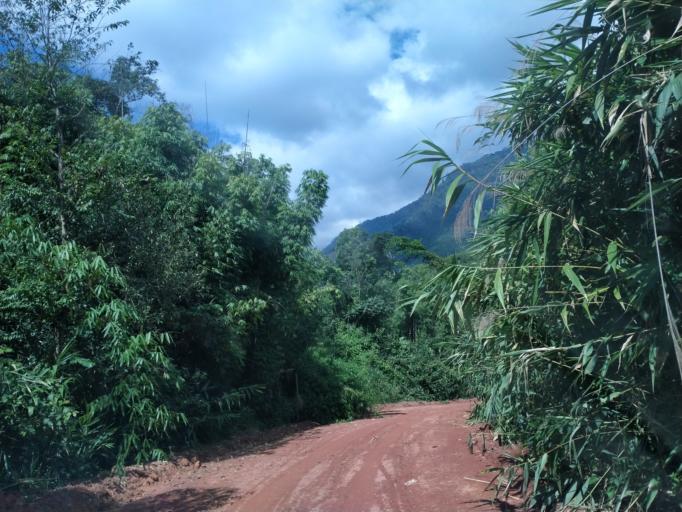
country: LA
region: Vientiane
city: Muang Phon-Hong
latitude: 18.6424
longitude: 102.9023
